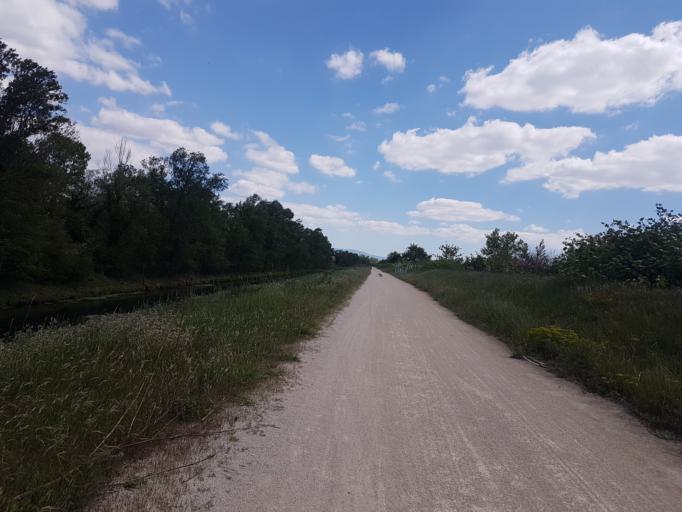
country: FR
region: Rhone-Alpes
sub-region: Departement de la Drome
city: La Roche-de-Glun
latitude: 45.0234
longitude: 4.8462
